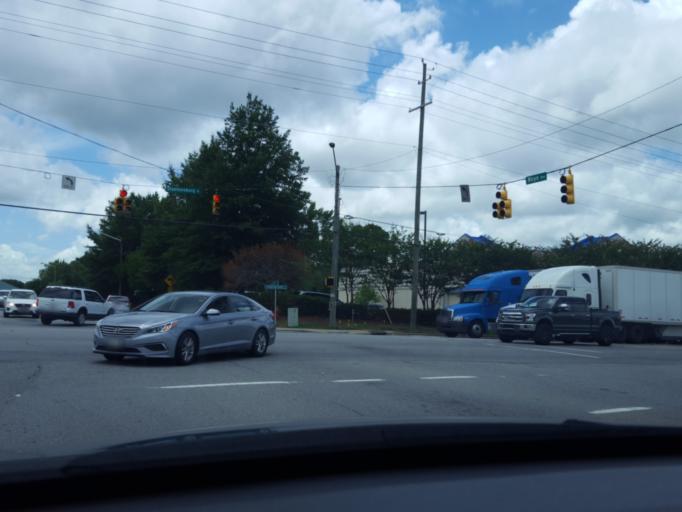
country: US
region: North Carolina
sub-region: Pitt County
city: Greenville
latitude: 35.6061
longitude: -77.4009
